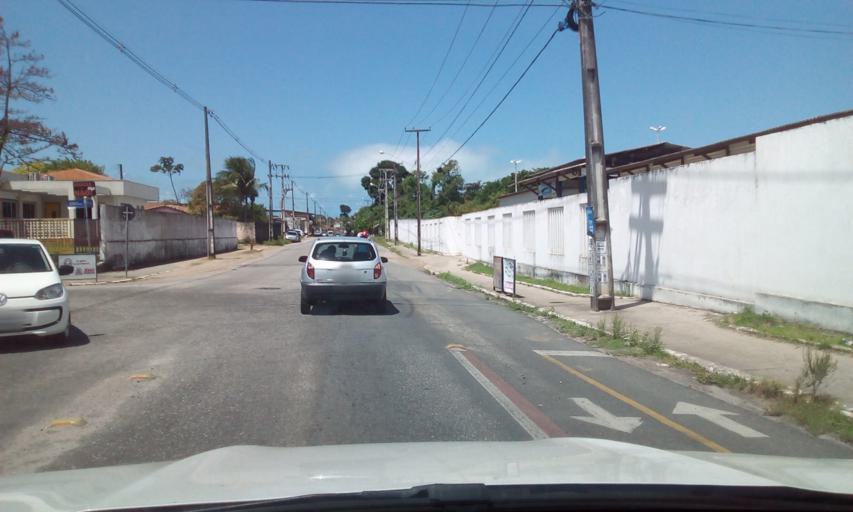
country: BR
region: Paraiba
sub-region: Joao Pessoa
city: Joao Pessoa
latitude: -7.1711
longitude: -34.8345
